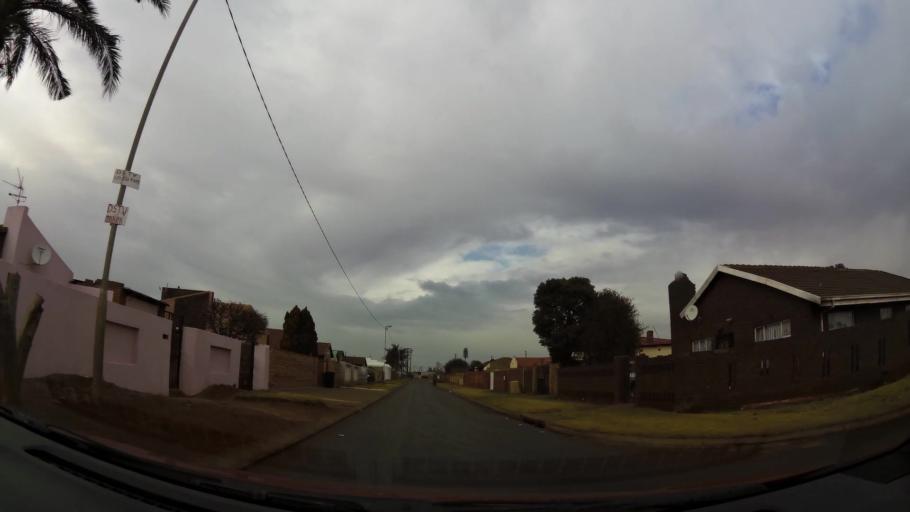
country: ZA
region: Gauteng
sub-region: City of Johannesburg Metropolitan Municipality
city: Soweto
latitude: -26.2890
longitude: 27.8399
